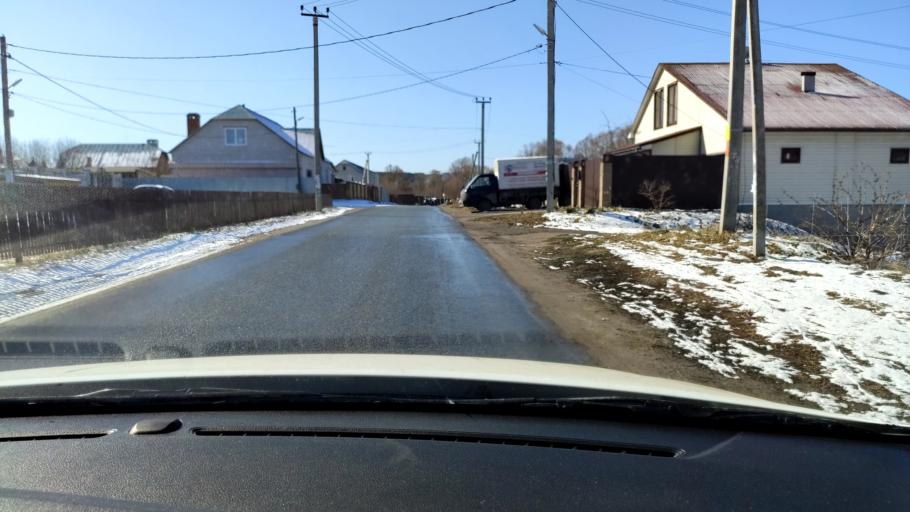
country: RU
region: Tatarstan
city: Vysokaya Gora
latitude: 55.8728
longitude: 49.2439
